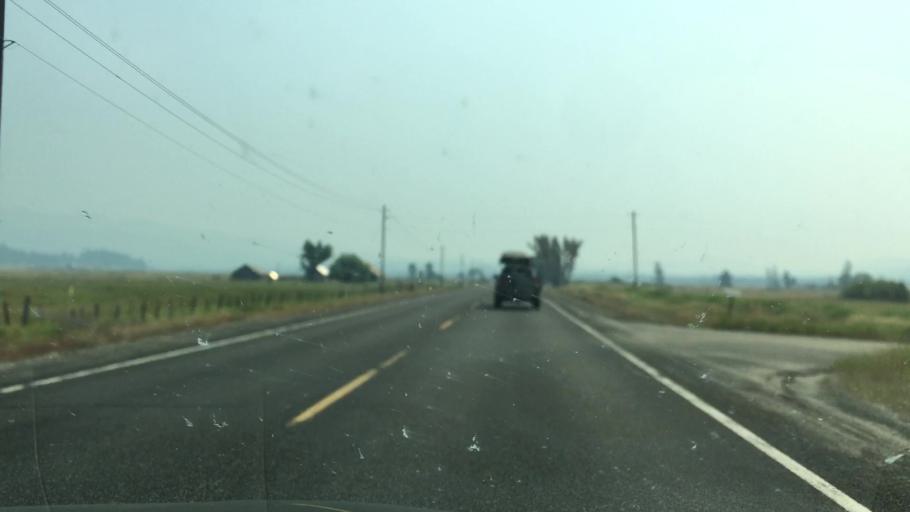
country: US
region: Idaho
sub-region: Valley County
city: Cascade
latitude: 44.4352
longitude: -115.9994
